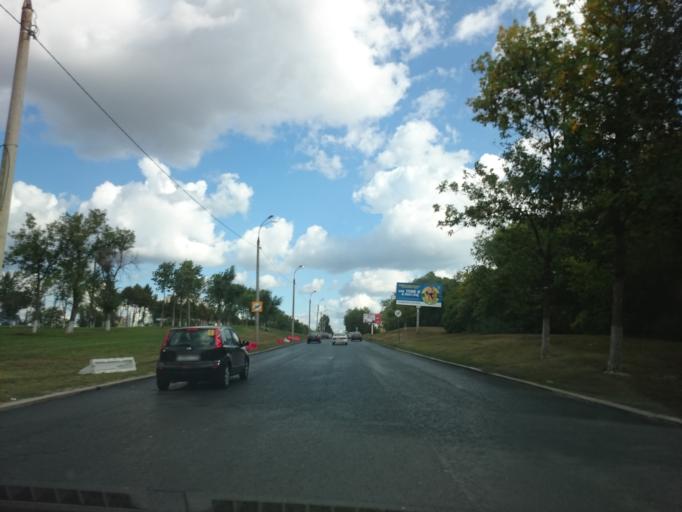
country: RU
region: Samara
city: Samara
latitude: 53.2270
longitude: 50.1750
